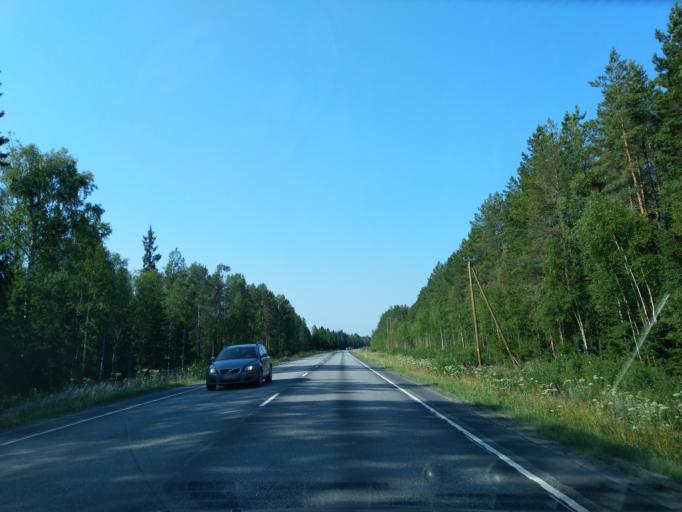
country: FI
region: Satakunta
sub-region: Pori
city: Pomarkku
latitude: 61.7128
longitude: 22.0392
